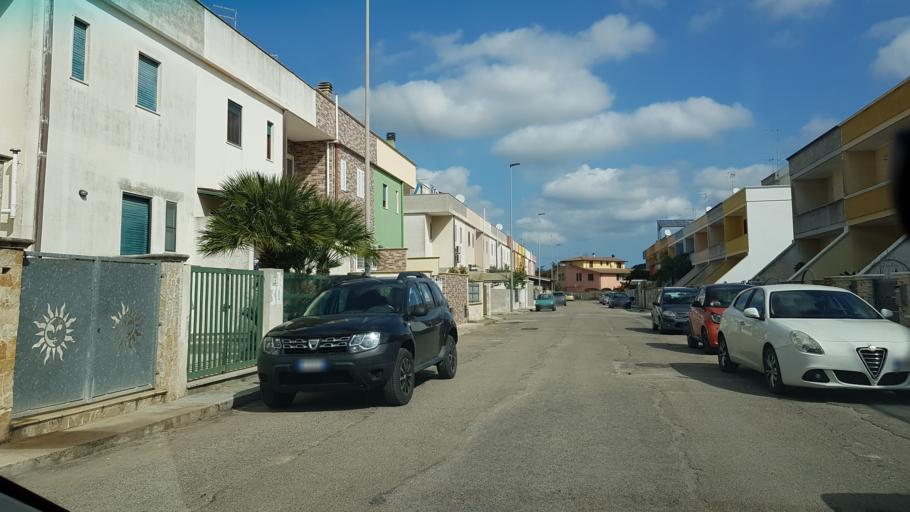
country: IT
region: Apulia
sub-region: Provincia di Brindisi
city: San Pietro Vernotico
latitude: 40.4775
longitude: 17.9995
